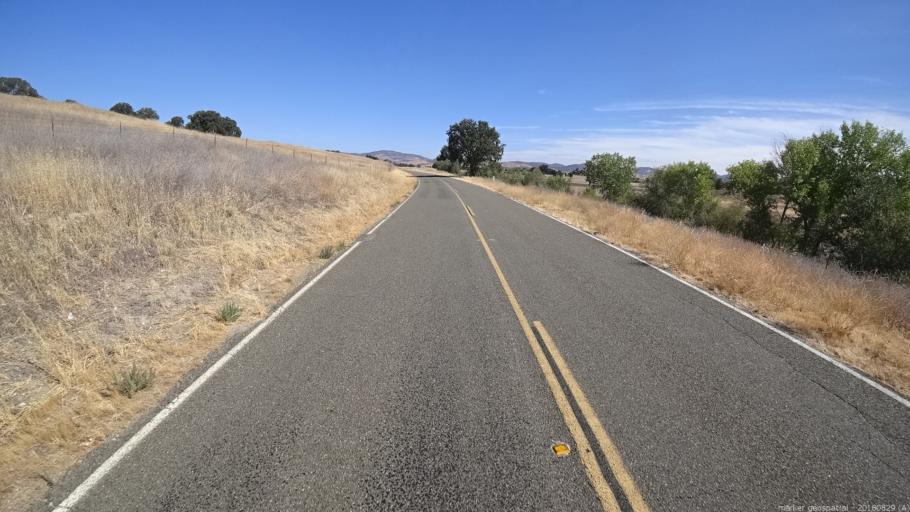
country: US
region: California
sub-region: San Luis Obispo County
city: Lake Nacimiento
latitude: 35.9173
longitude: -121.0843
